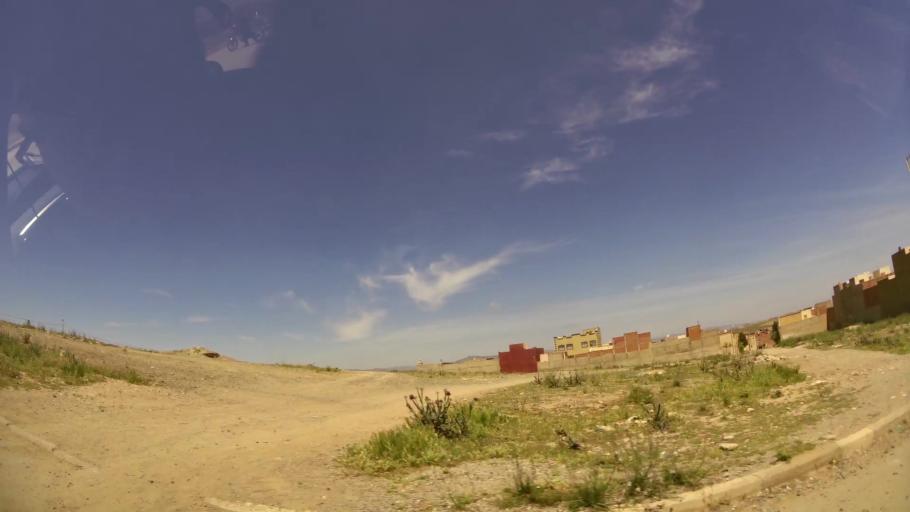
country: MA
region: Oriental
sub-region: Oujda-Angad
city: Oujda
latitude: 34.6525
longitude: -1.9478
